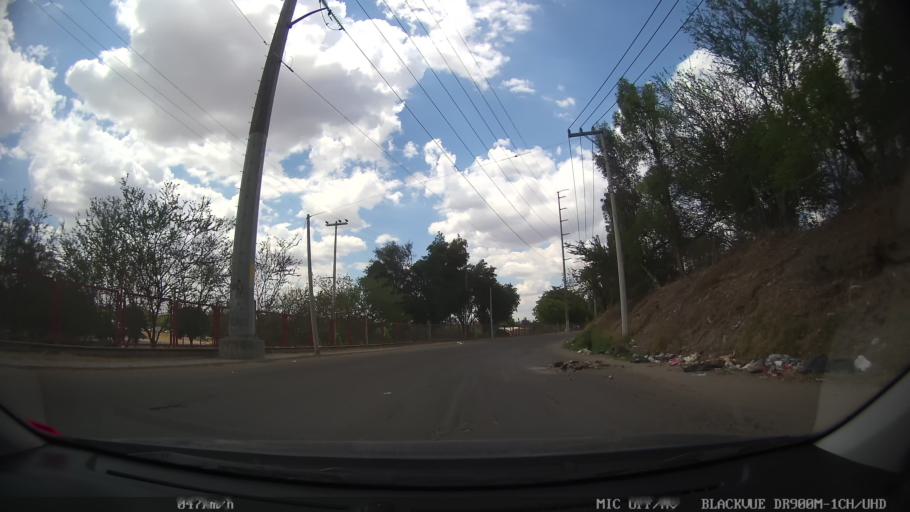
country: MX
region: Jalisco
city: Tlaquepaque
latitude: 20.6583
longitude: -103.2678
